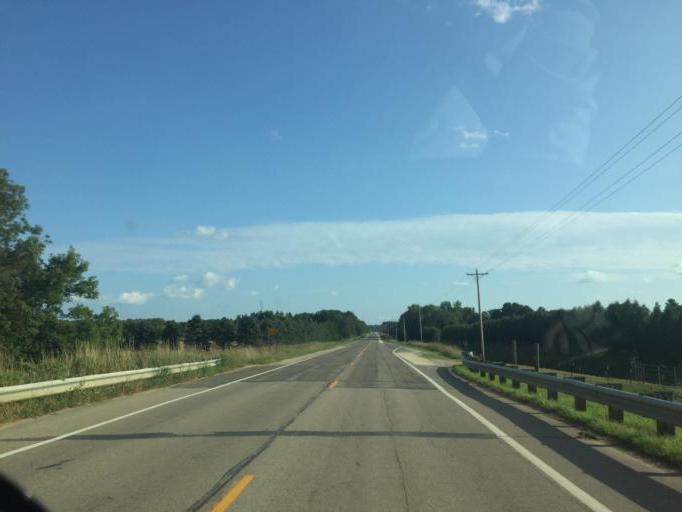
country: US
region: Minnesota
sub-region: Olmsted County
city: Rochester
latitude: 43.9788
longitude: -92.5582
